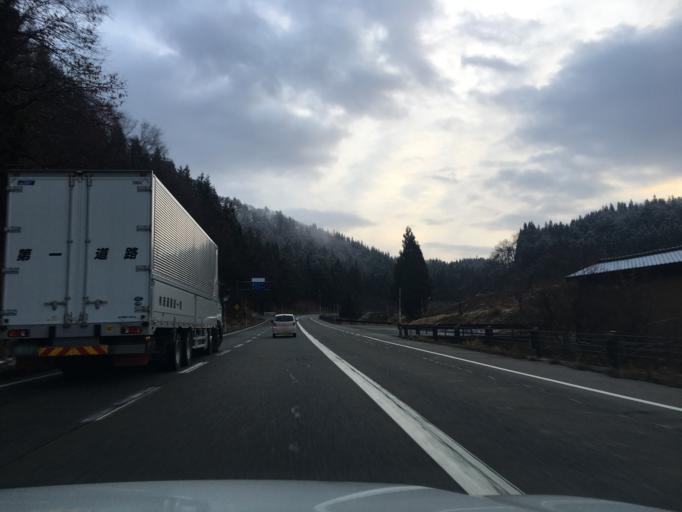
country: JP
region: Niigata
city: Murakami
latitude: 38.4239
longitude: 139.5715
